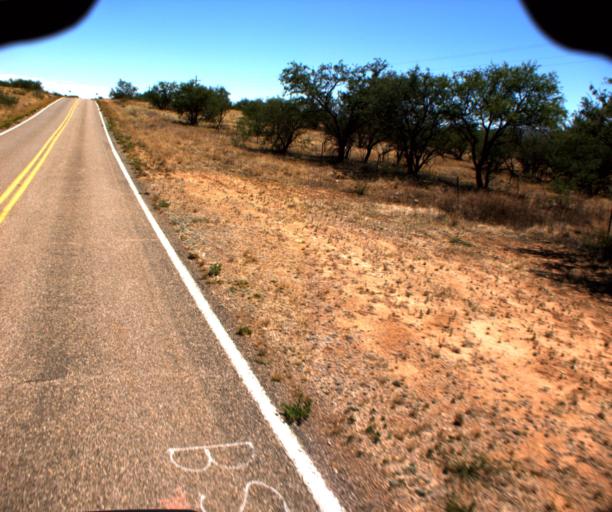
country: US
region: Arizona
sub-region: Pima County
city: Sells
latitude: 31.5714
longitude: -111.5380
